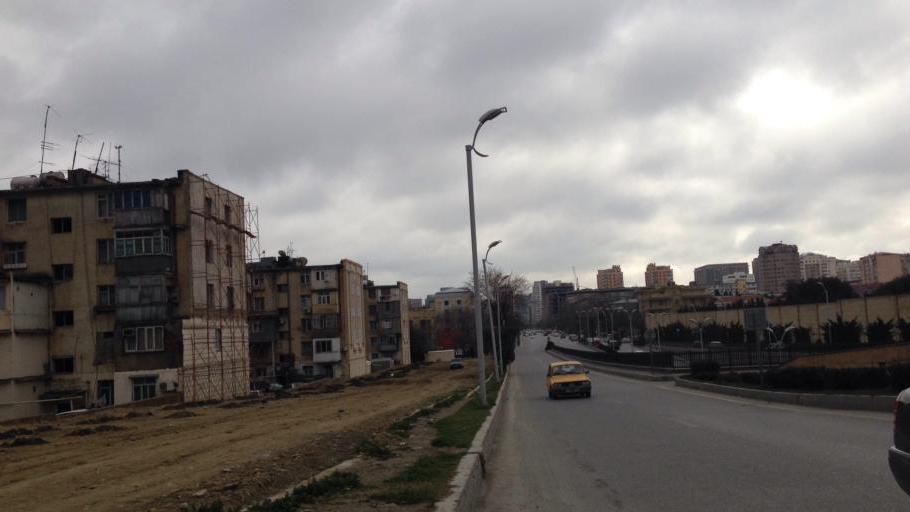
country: AZ
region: Baki
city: Bilajari
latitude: 40.4094
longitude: 49.8355
